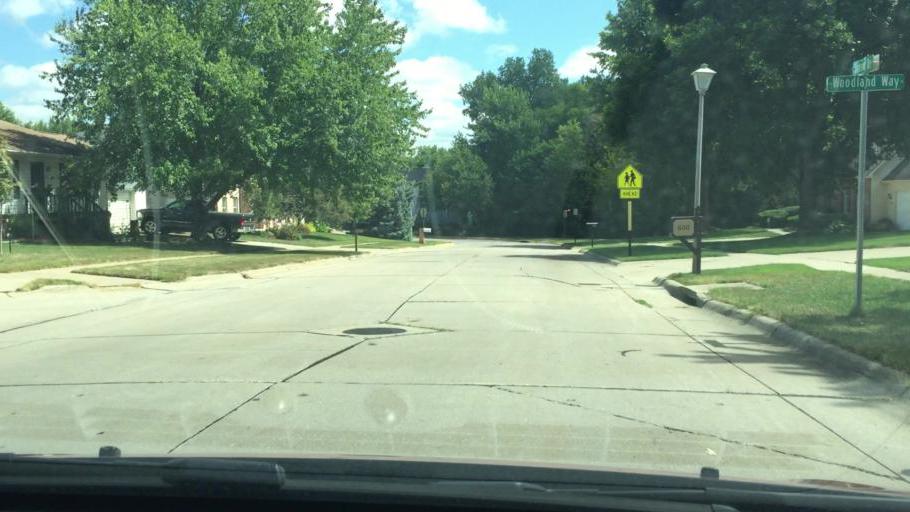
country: US
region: Iowa
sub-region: Muscatine County
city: Muscatine
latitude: 41.4413
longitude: -91.0572
